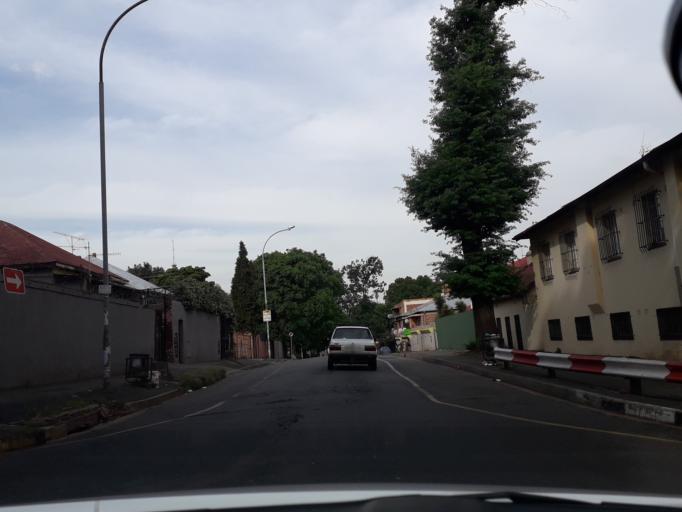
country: ZA
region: Gauteng
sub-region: City of Johannesburg Metropolitan Municipality
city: Johannesburg
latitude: -26.1901
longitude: 28.0672
